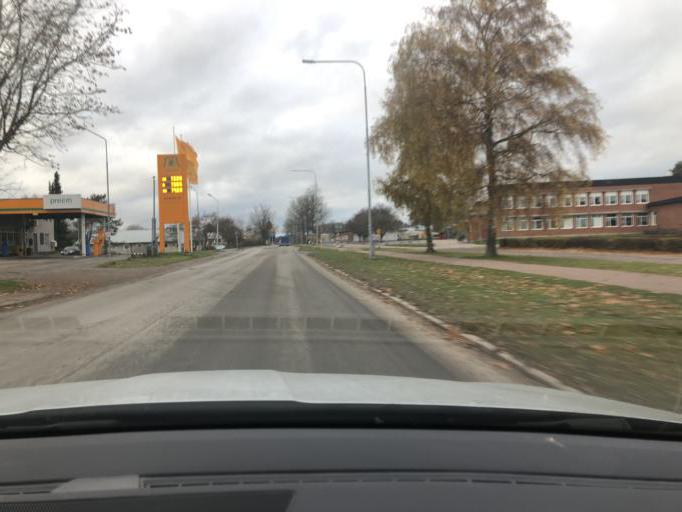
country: SE
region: Uppsala
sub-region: Tierps Kommun
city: Tierp
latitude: 60.3440
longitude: 17.5078
